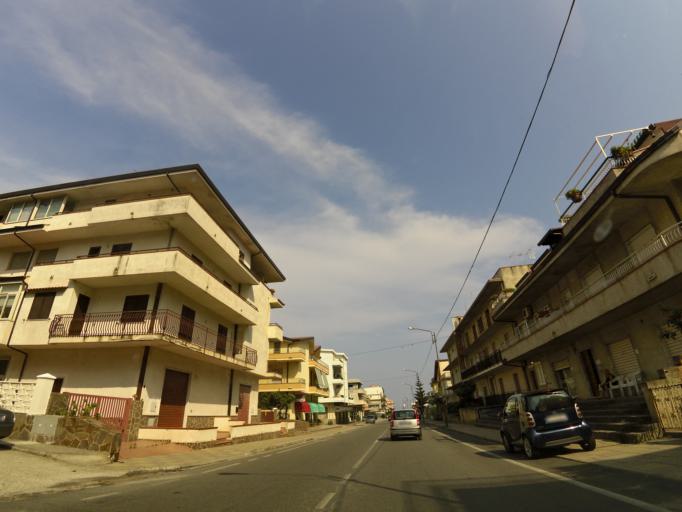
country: IT
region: Calabria
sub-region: Provincia di Reggio Calabria
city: Monasterace Marina
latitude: 38.4348
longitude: 16.5685
